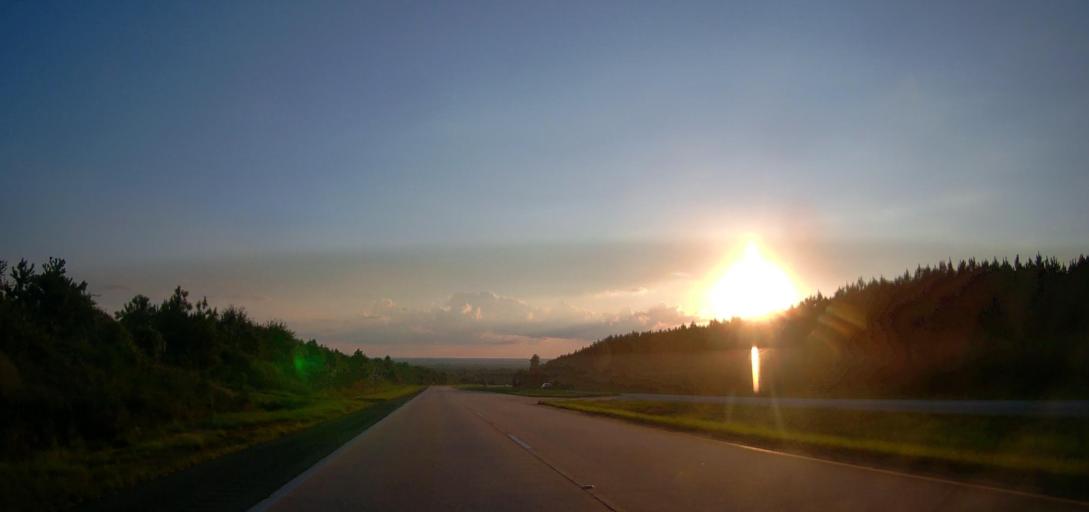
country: US
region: Georgia
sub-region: Peach County
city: Fort Valley
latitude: 32.5475
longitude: -83.9863
